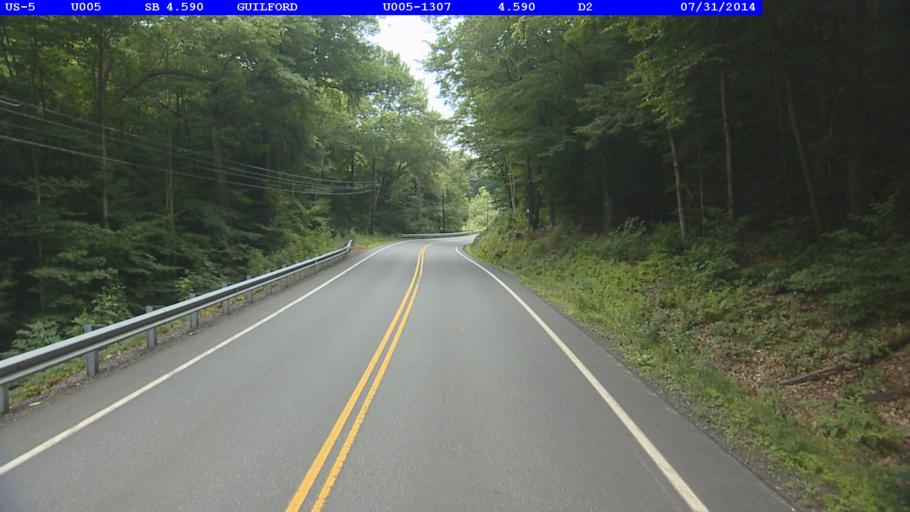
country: US
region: Vermont
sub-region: Windham County
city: Brattleboro
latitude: 42.7937
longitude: -72.5643
